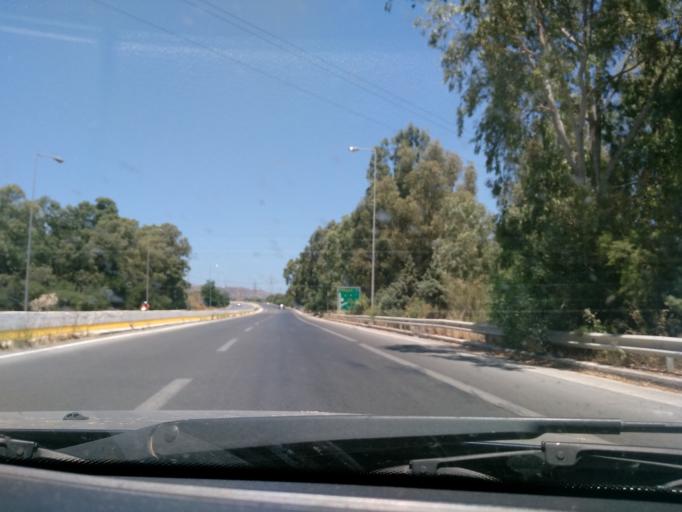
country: GR
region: Crete
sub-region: Nomos Irakleiou
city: Gazi
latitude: 35.3330
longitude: 25.0522
